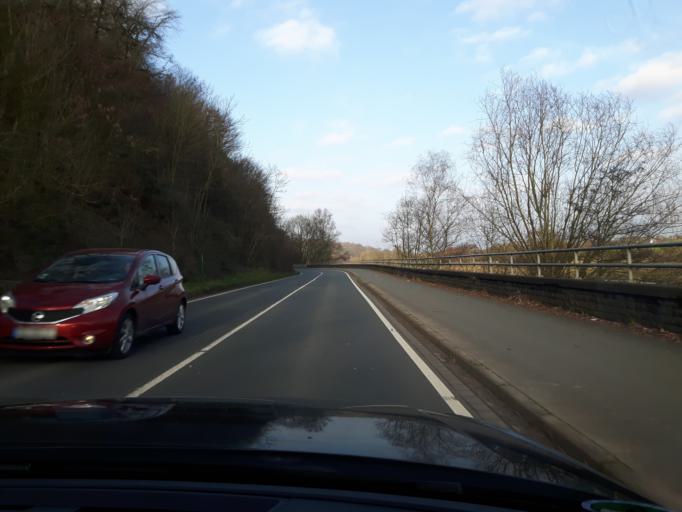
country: DE
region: North Rhine-Westphalia
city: Hattingen
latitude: 51.3885
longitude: 7.1553
